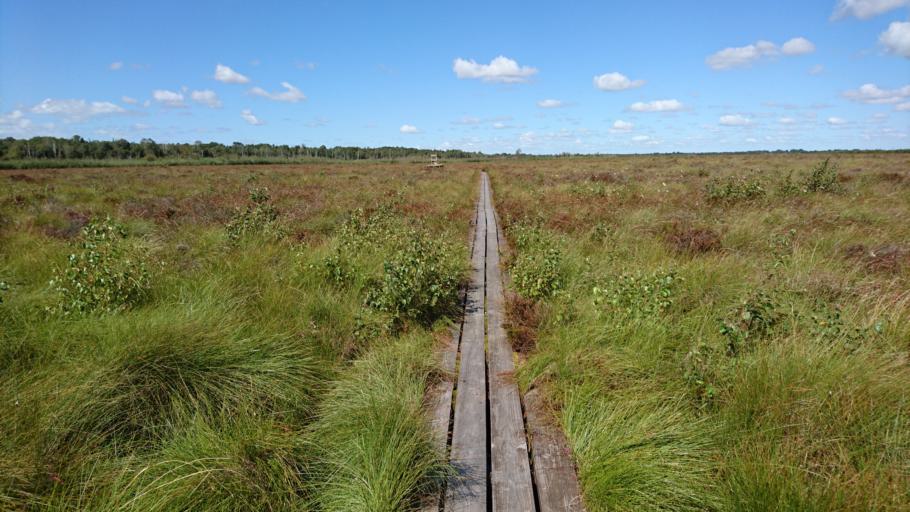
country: DK
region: North Denmark
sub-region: Alborg Kommune
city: Storvorde
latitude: 56.9124
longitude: 10.1864
